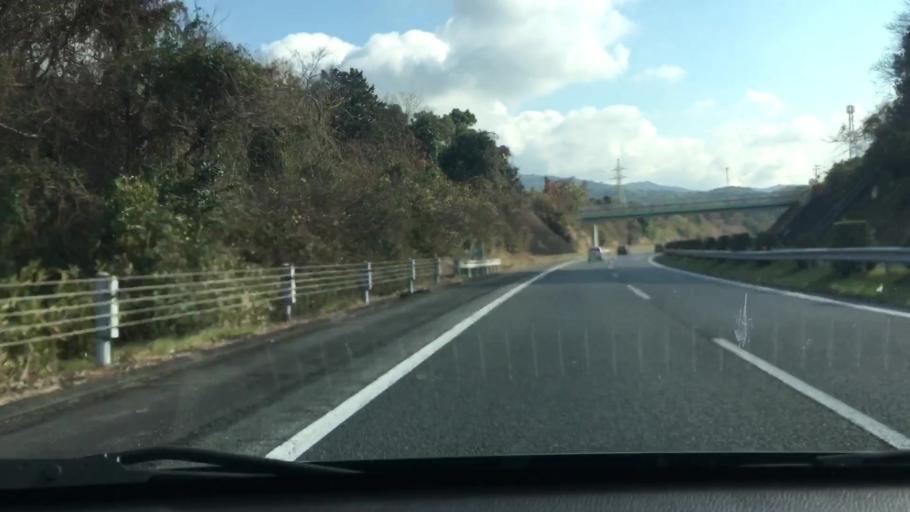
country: JP
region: Kumamoto
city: Matsubase
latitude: 32.6383
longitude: 130.7087
